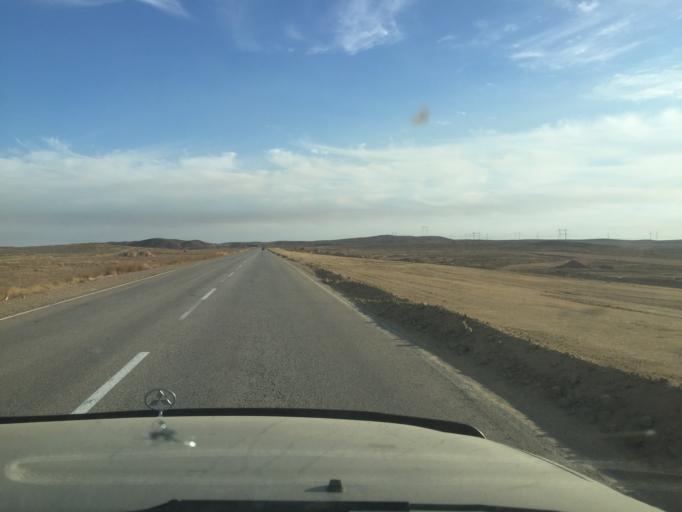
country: KZ
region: Zhambyl
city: Mynaral
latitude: 45.5202
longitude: 73.4890
